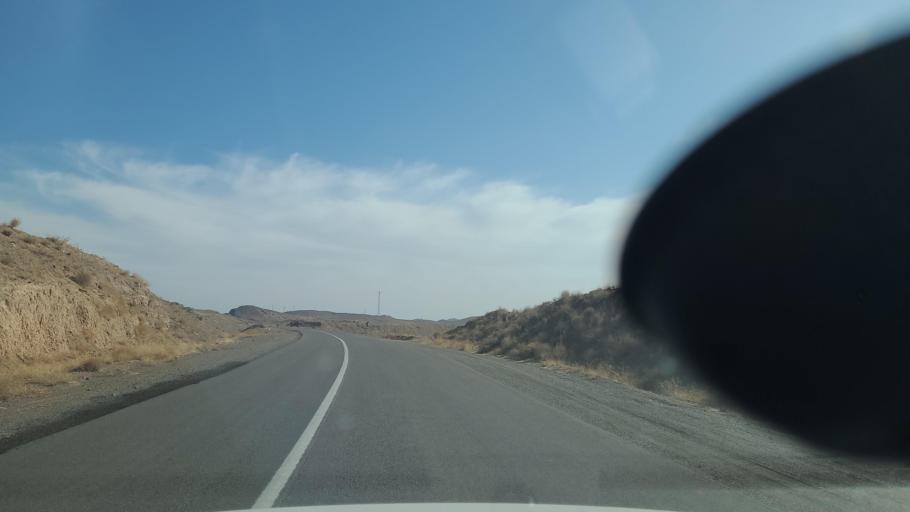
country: IR
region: Razavi Khorasan
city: Fariman
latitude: 35.5956
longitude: 59.7080
